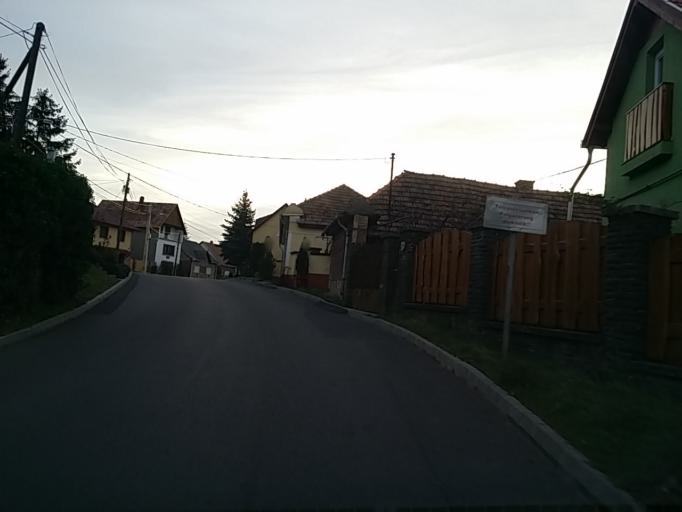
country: HU
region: Heves
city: Abasar
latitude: 47.8166
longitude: 19.9904
